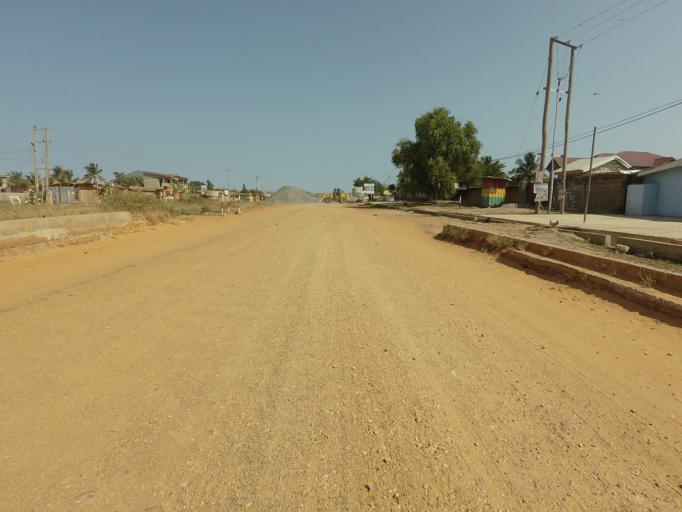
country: GH
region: Greater Accra
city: Teshi Old Town
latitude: 5.6098
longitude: -0.1234
